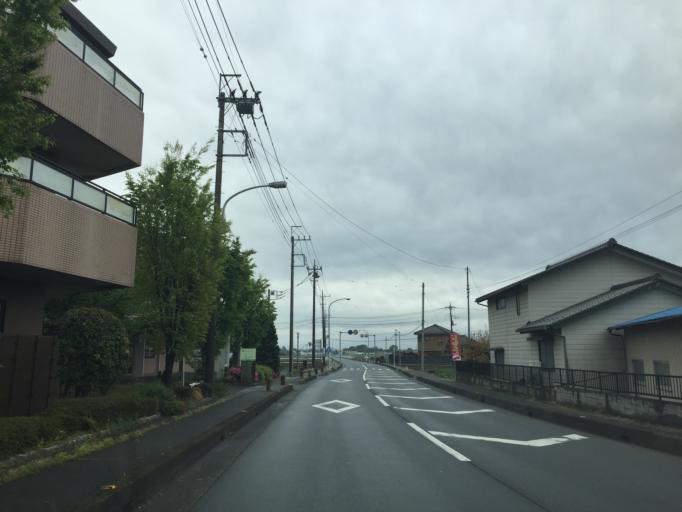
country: JP
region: Saitama
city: Shiki
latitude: 35.8716
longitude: 139.5635
